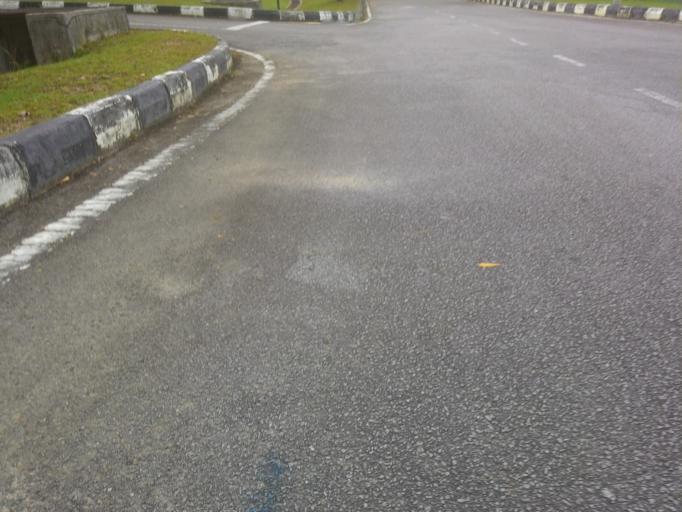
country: MY
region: Kedah
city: Kulim
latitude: 5.3816
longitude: 100.5769
